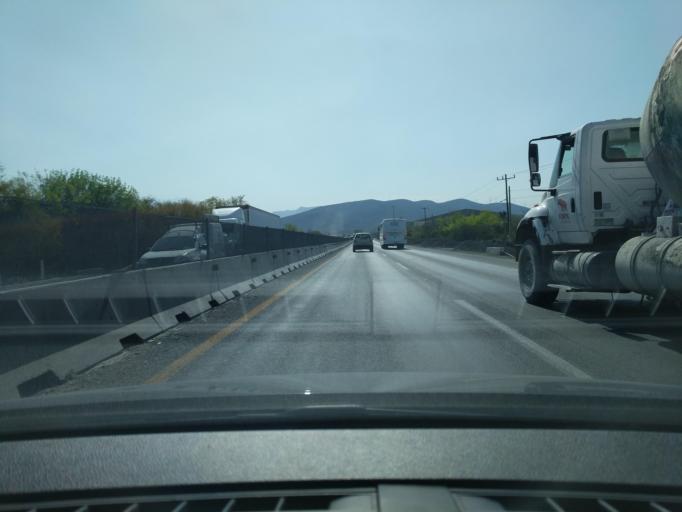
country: MX
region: Nuevo Leon
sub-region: Garcia
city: Los Parques
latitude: 25.7705
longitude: -100.4764
